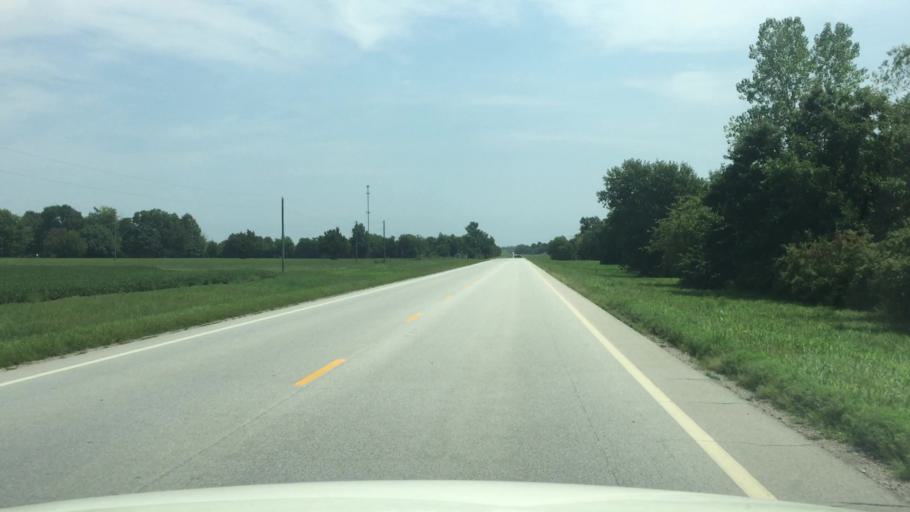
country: US
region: Kansas
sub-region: Cherokee County
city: Columbus
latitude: 37.1787
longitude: -94.8643
